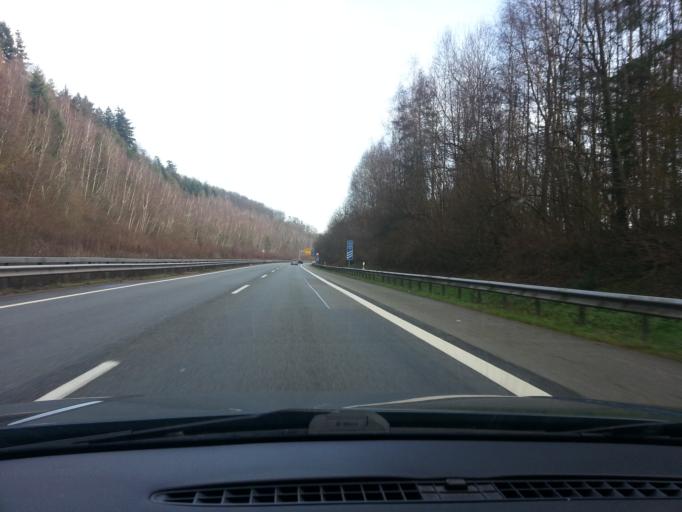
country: DE
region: Rheinland-Pfalz
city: Hoheischweiler
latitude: 49.2174
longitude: 7.5315
